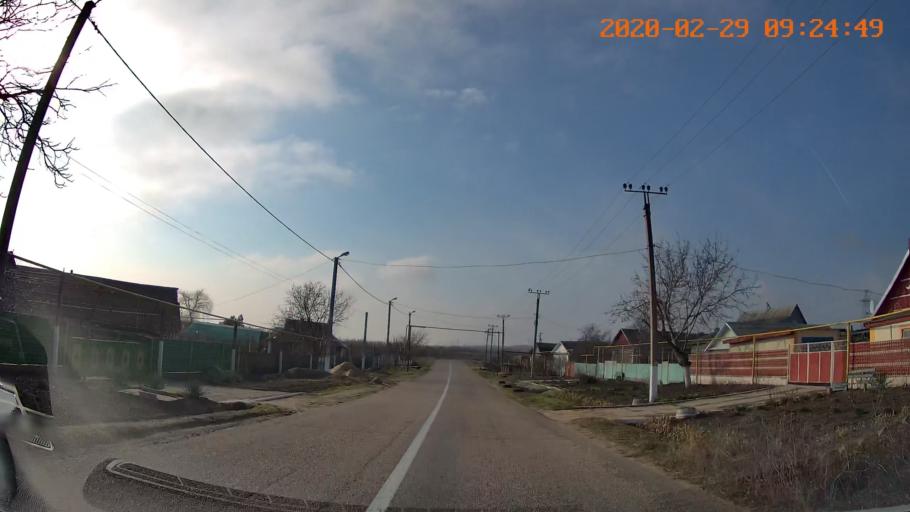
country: MD
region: Telenesti
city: Pervomaisc
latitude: 46.7124
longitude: 29.9576
